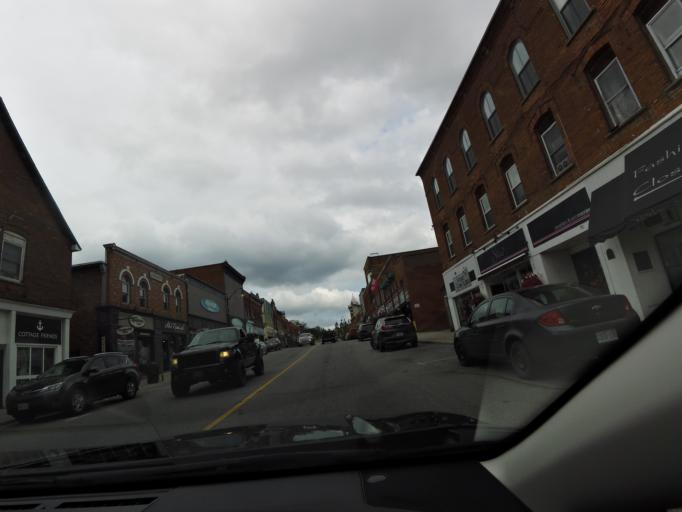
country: CA
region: Ontario
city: Bracebridge
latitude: 45.0405
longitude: -79.3089
